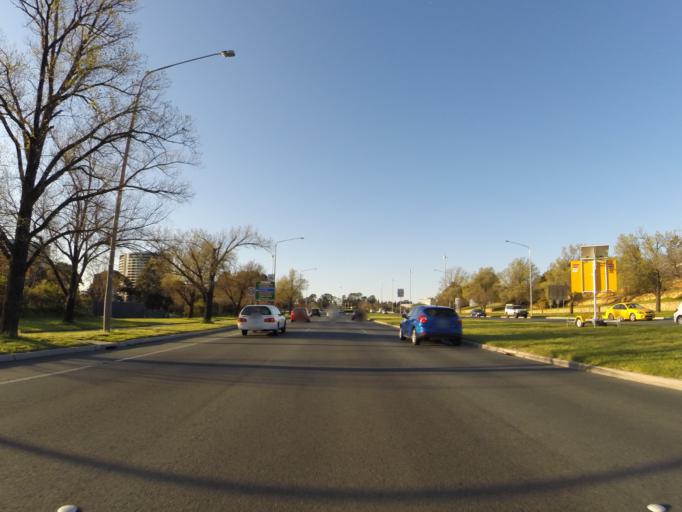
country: AU
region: Australian Capital Territory
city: Canberra
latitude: -35.2881
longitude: 149.1275
